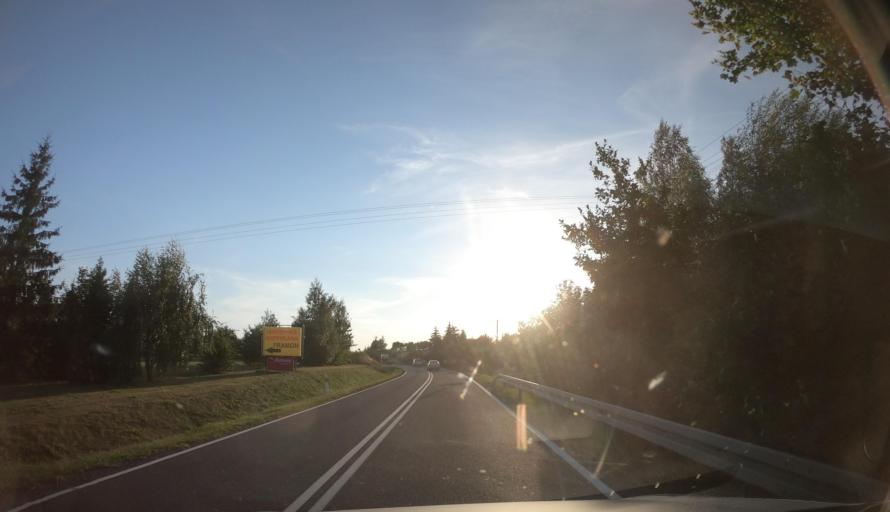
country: PL
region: Kujawsko-Pomorskie
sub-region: Powiat swiecki
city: Swiekatowo
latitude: 53.3052
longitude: 18.0785
